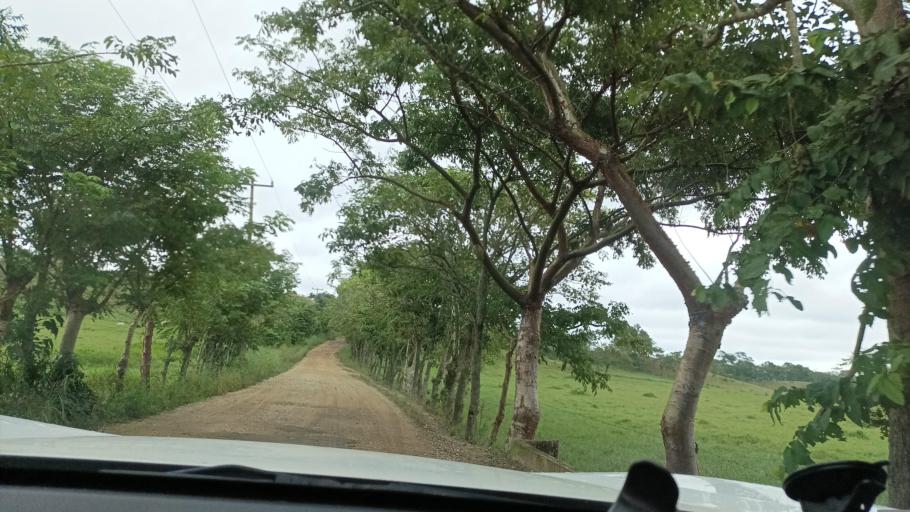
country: MX
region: Veracruz
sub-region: Moloacan
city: Cuichapa
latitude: 17.7939
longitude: -94.3812
